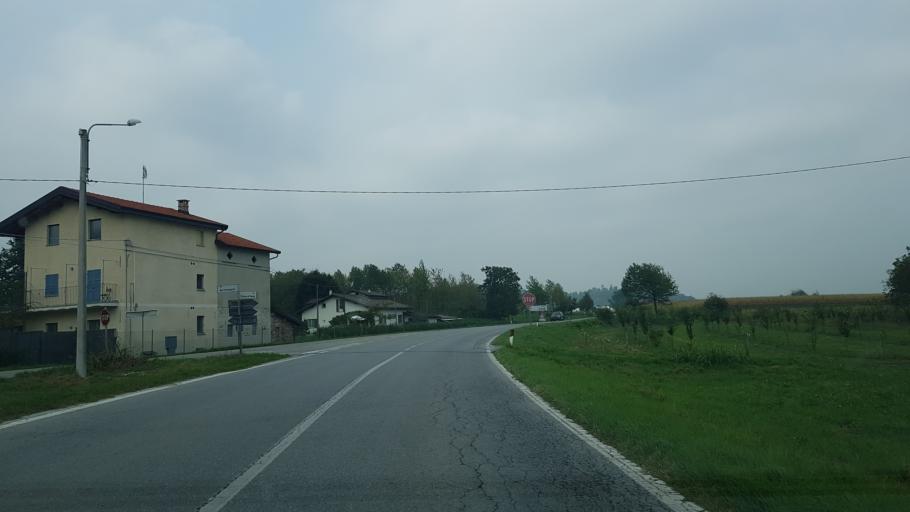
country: IT
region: Piedmont
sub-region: Provincia di Cuneo
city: Peveragno
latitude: 44.3274
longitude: 7.6397
